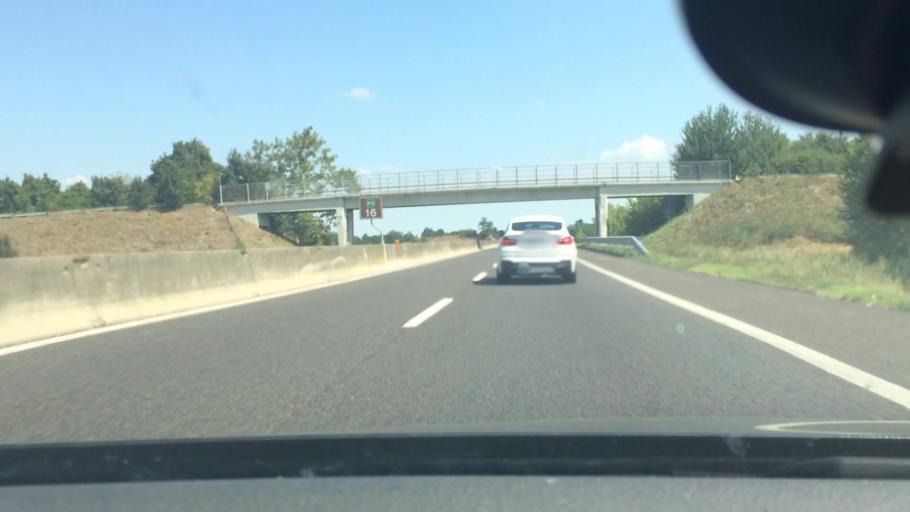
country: IT
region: Emilia-Romagna
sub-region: Provincia di Bologna
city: Bentivoglio
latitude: 44.6499
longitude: 11.4451
